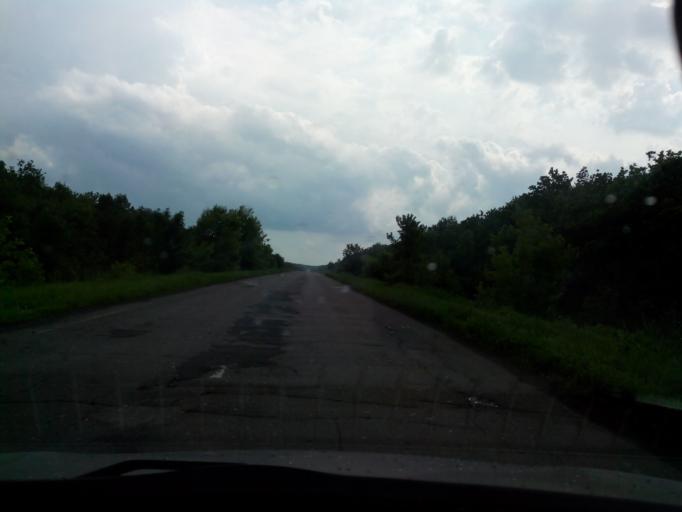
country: RU
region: Volgograd
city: Mikhaylovka
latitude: 49.9085
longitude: 42.9371
